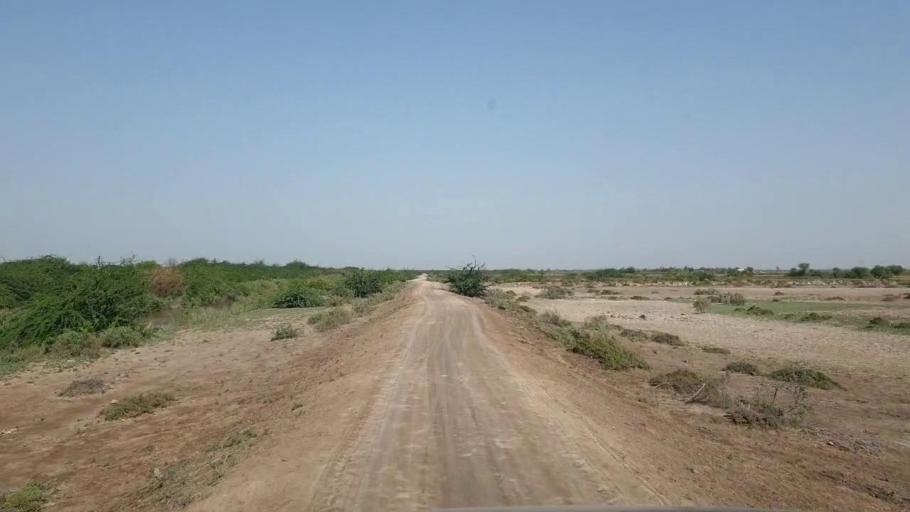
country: PK
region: Sindh
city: Tando Bago
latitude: 24.6515
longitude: 69.0708
